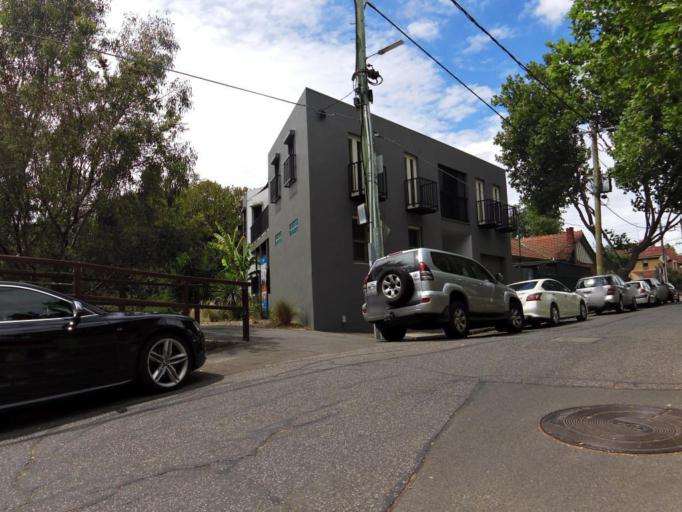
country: AU
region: Victoria
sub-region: Port Phillip
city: Elwood
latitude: -37.8855
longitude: 144.9907
